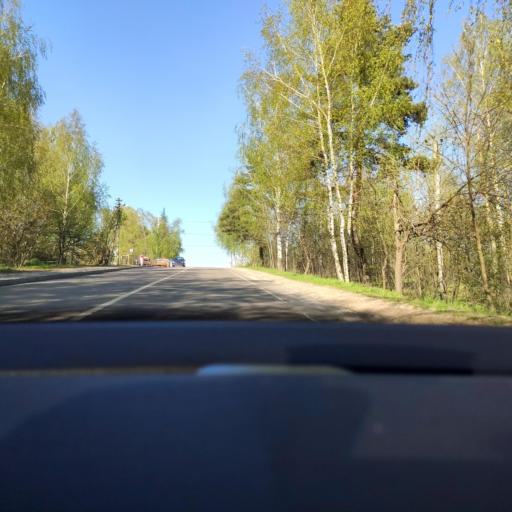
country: RU
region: Moskovskaya
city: Dmitrov
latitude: 56.3555
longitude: 37.5557
